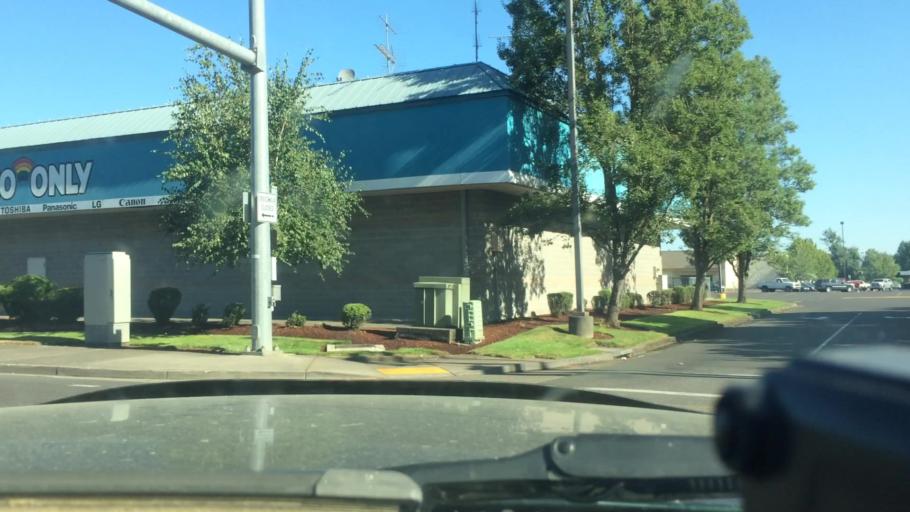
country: US
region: Oregon
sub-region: Lane County
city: Eugene
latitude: 44.0901
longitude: -123.0659
